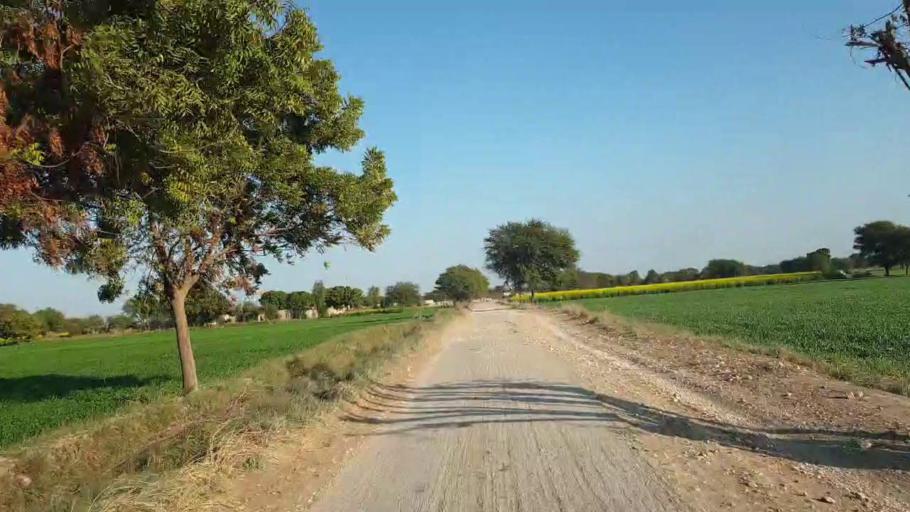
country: PK
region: Sindh
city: Shahpur Chakar
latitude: 26.1272
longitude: 68.5561
